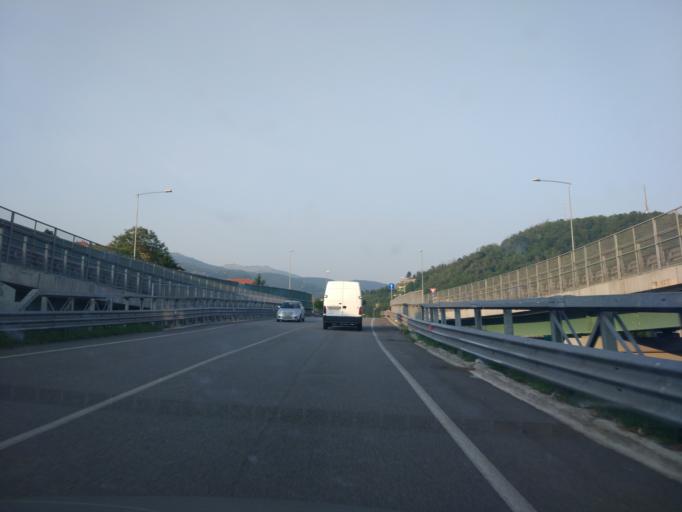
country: IT
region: Lombardy
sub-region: Provincia di Como
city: Como
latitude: 45.7871
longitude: 9.0846
